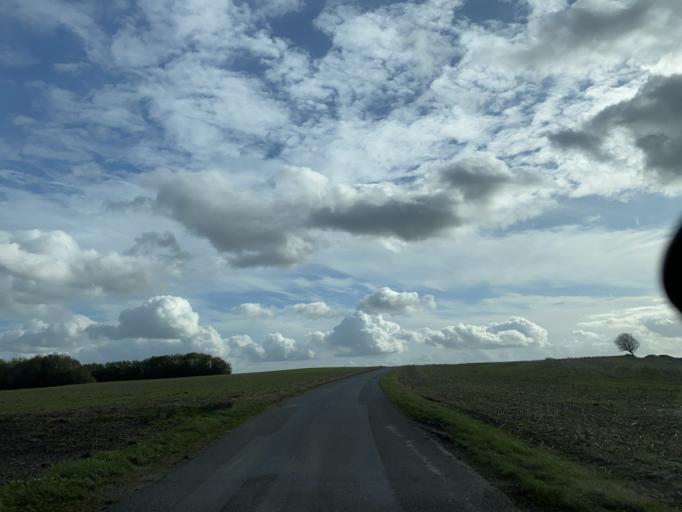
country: DK
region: Central Jutland
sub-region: Arhus Kommune
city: Sabro
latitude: 56.2058
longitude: 9.9908
